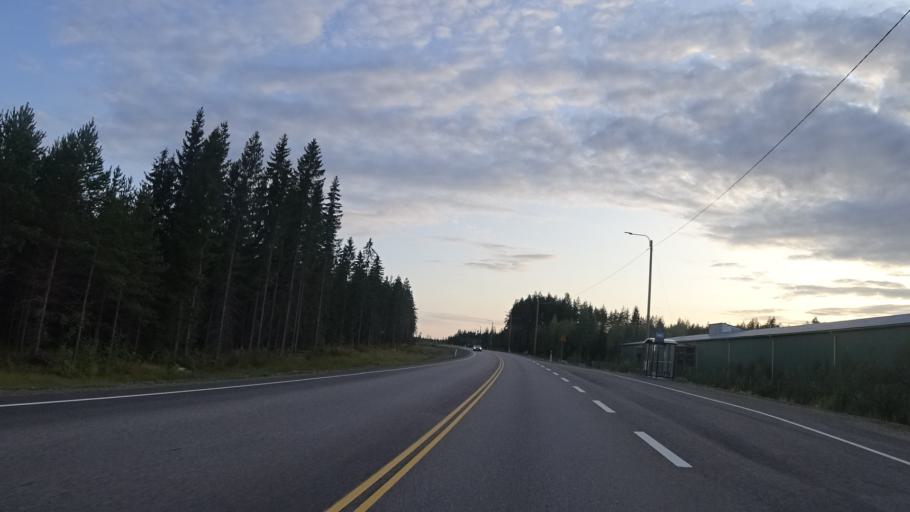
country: FI
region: Kymenlaakso
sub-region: Kotka-Hamina
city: Miehikkaelae
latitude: 60.6357
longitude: 27.8559
